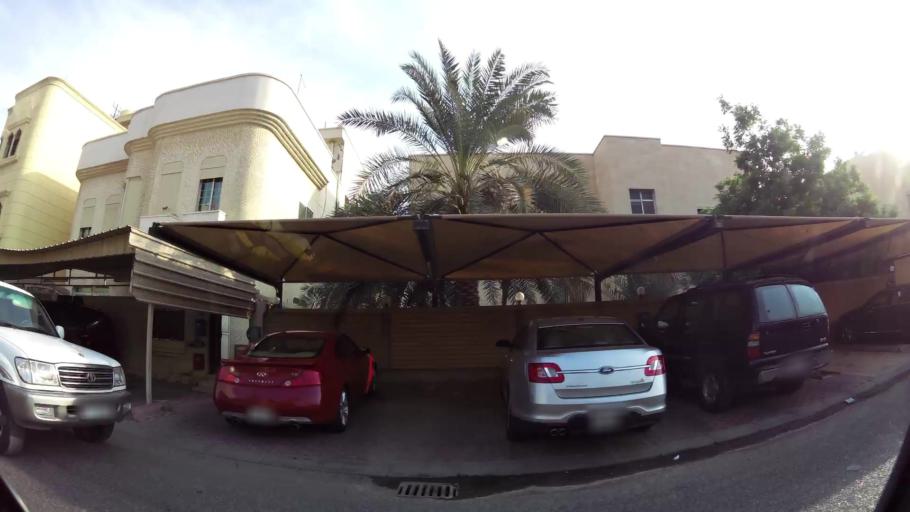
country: KW
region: Muhafazat Hawalli
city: Hawalli
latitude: 29.3084
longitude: 48.0137
